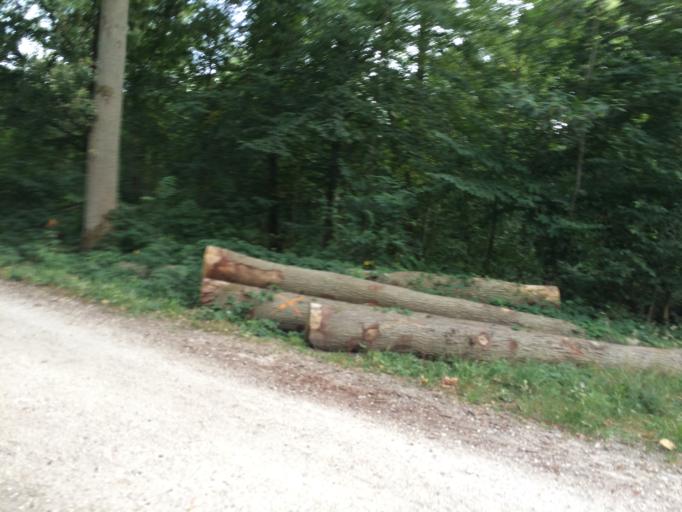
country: FR
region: Ile-de-France
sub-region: Departement de l'Essonne
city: Quincy-sous-Senart
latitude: 48.6537
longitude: 2.5383
